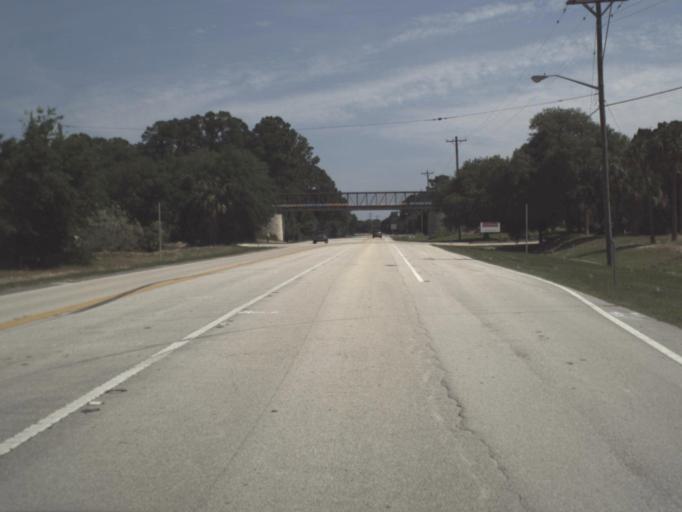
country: US
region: Florida
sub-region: Duval County
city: Atlantic Beach
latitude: 30.3913
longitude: -81.4576
